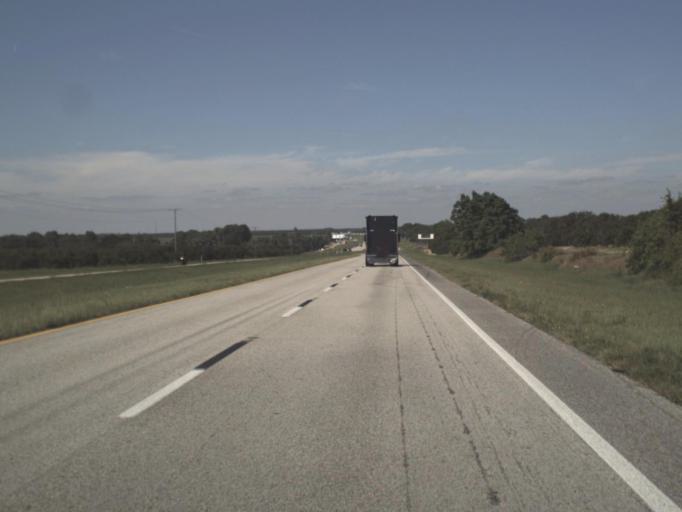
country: US
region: Florida
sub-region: Highlands County
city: Lake Placid
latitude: 27.3381
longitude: -81.3858
